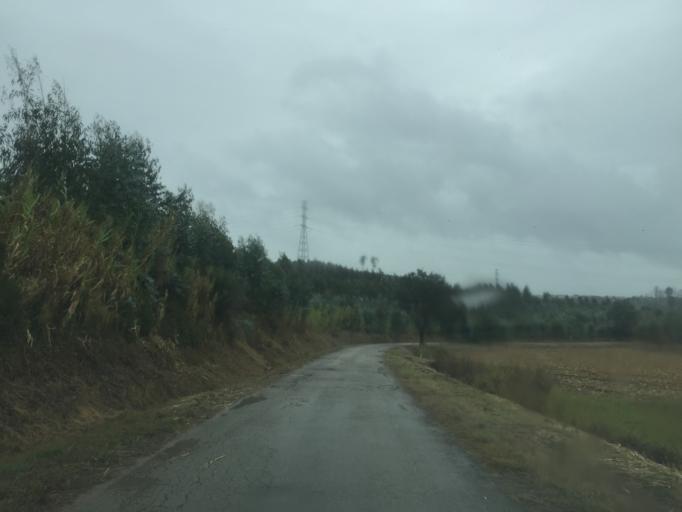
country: PT
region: Coimbra
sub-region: Figueira da Foz
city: Lavos
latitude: 40.0843
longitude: -8.8005
